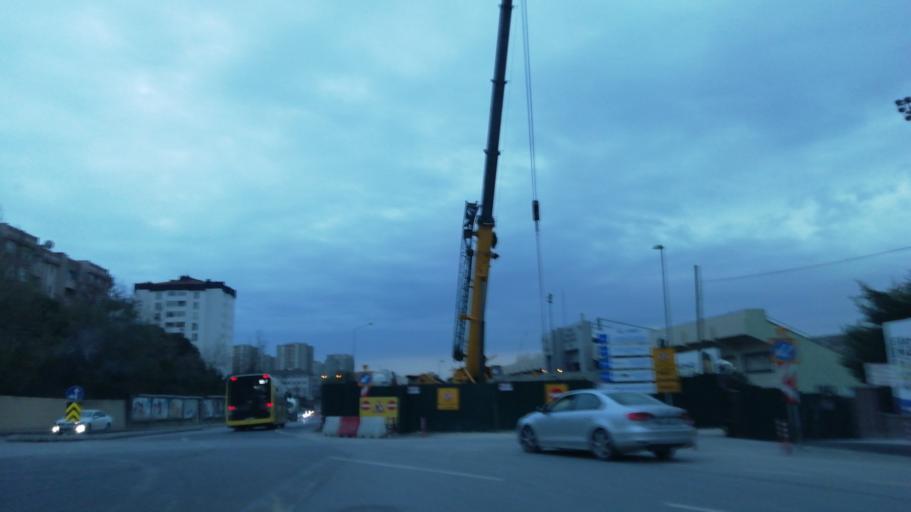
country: TR
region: Istanbul
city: Basaksehir
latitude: 41.0571
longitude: 28.7745
